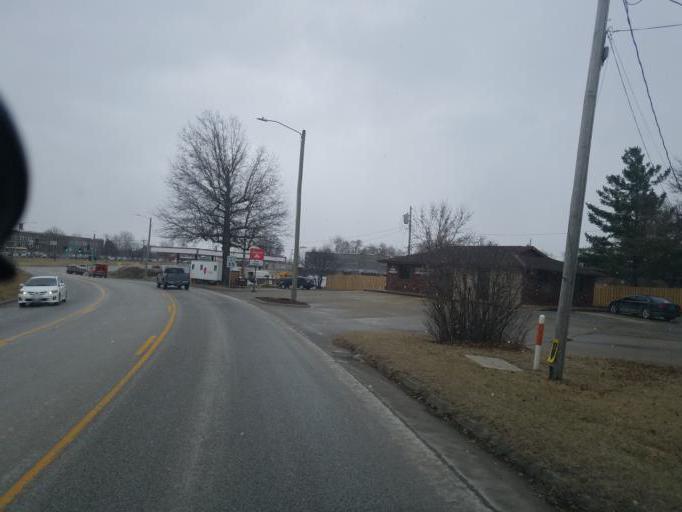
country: US
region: Missouri
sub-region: Macon County
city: Macon
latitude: 39.7465
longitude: -92.4675
